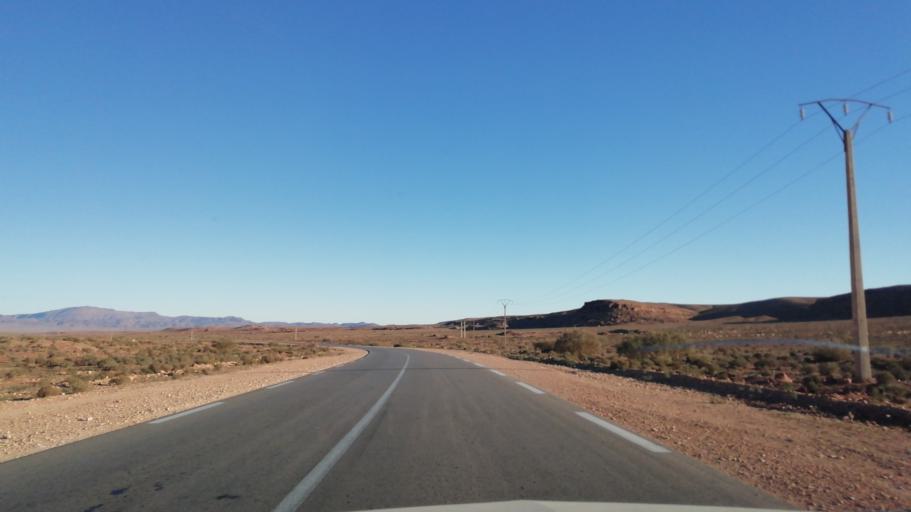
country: DZ
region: El Bayadh
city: El Abiodh Sidi Cheikh
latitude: 33.1686
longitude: 0.4606
